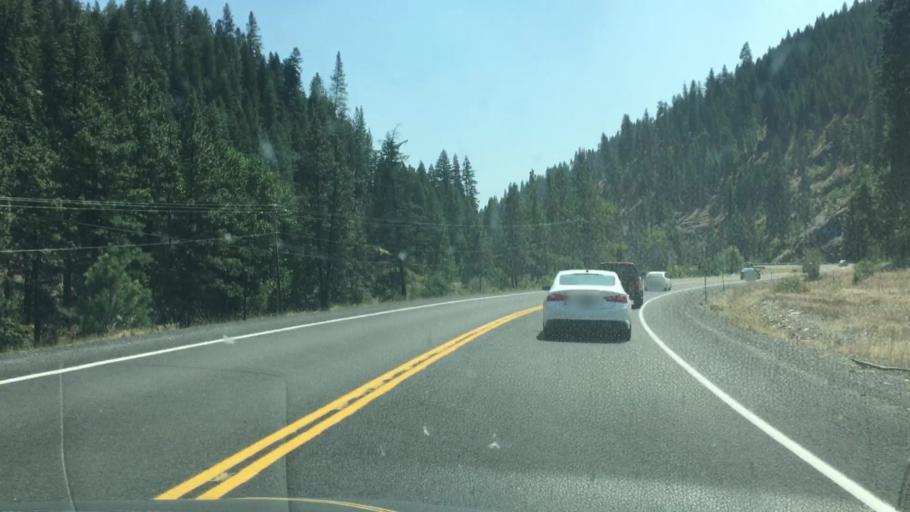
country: US
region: Idaho
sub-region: Valley County
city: McCall
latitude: 45.2024
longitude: -116.3108
